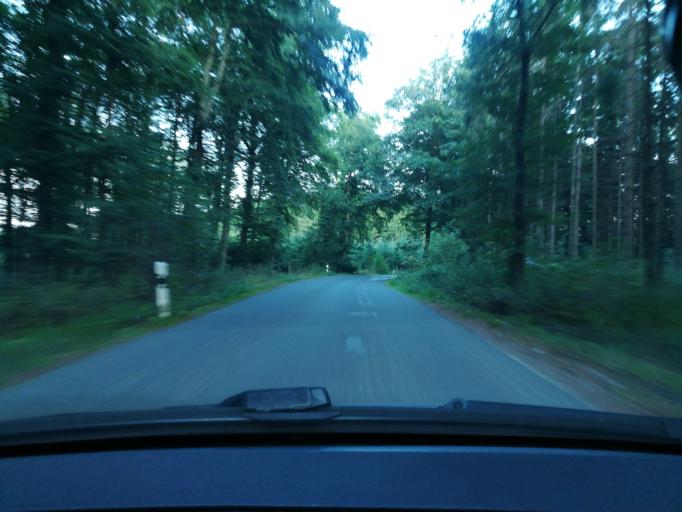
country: DE
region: North Rhine-Westphalia
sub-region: Regierungsbezirk Munster
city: Lienen
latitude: 52.1663
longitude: 7.9619
